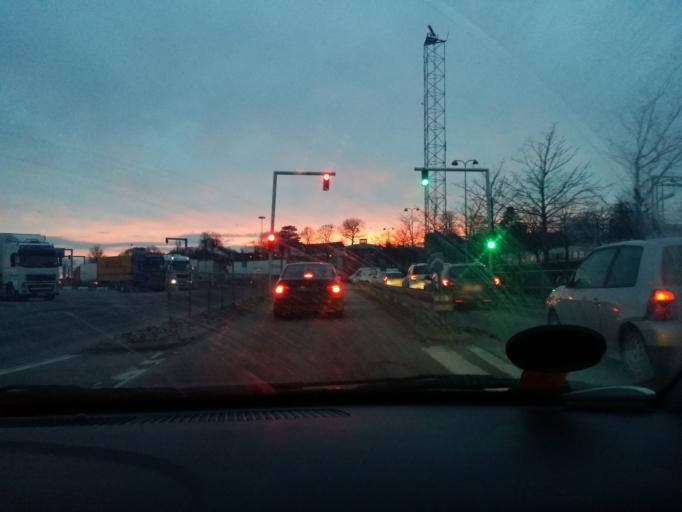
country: DK
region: Capital Region
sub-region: Helsingor Kommune
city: Helsingor
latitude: 56.0299
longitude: 12.6093
